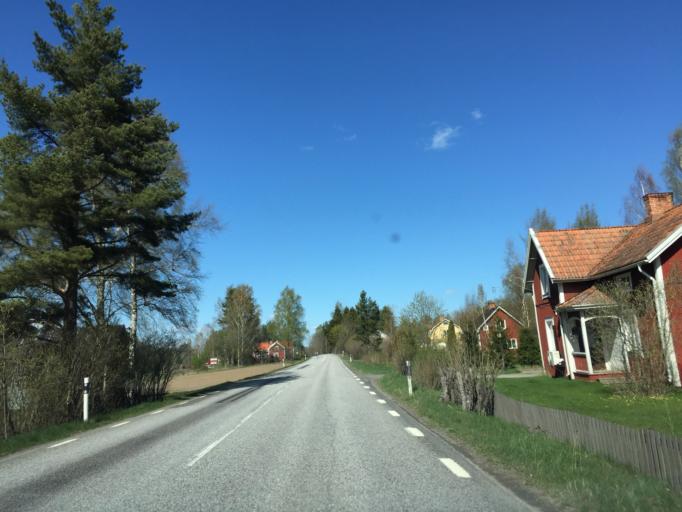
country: SE
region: OErebro
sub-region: Hallsbergs Kommun
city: Skollersta
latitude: 59.1027
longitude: 15.3271
